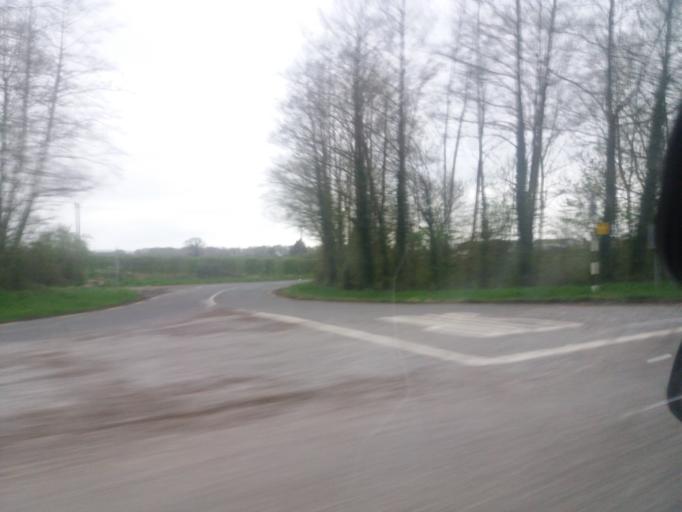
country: IE
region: Munster
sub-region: County Limerick
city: Rathkeale
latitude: 52.5286
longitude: -8.8967
